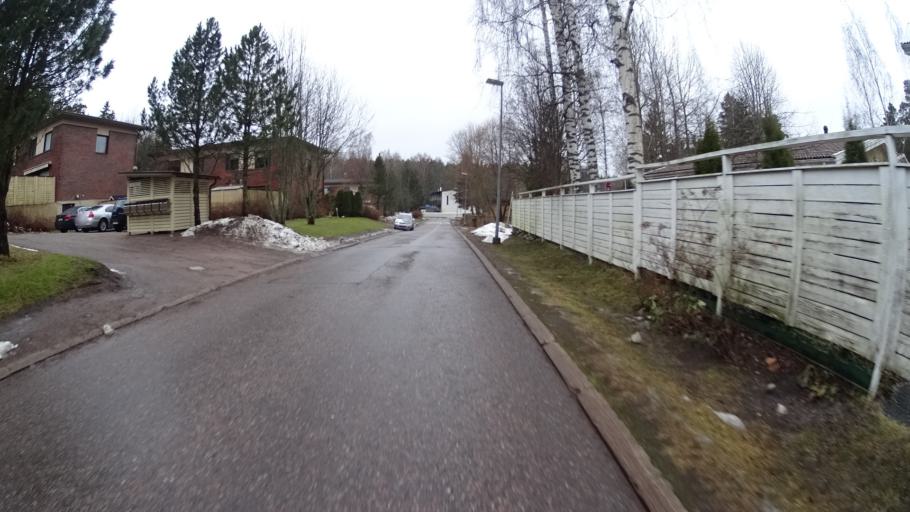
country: FI
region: Uusimaa
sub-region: Helsinki
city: Koukkuniemi
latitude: 60.1842
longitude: 24.7585
